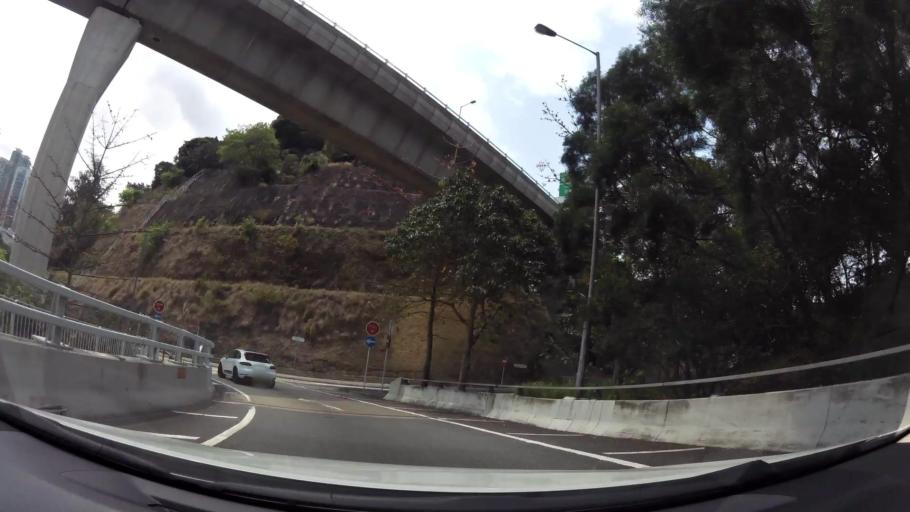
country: HK
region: Sham Shui Po
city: Sham Shui Po
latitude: 22.3404
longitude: 114.1427
